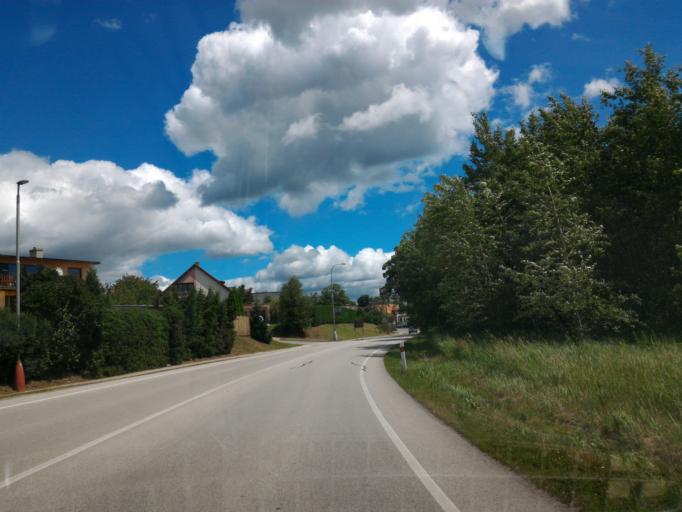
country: CZ
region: Vysocina
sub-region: Okres Jihlava
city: Trest'
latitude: 49.2825
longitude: 15.4770
